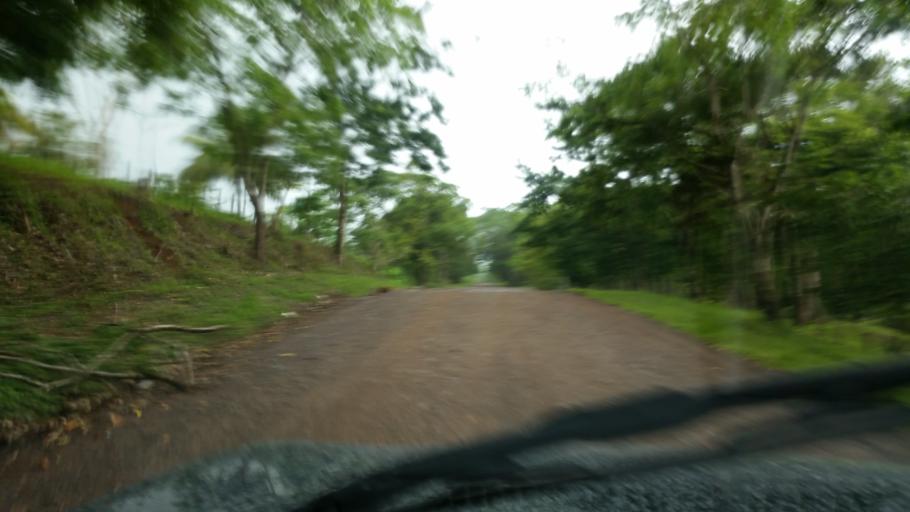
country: NI
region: Atlantico Norte (RAAN)
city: Siuna
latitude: 13.4093
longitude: -84.8539
